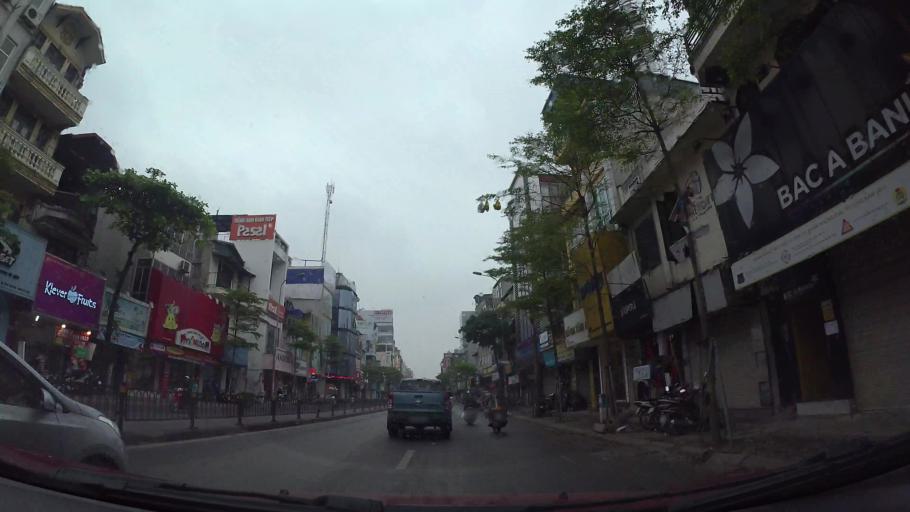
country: VN
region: Ha Noi
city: Dong Da
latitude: 21.0115
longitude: 105.8258
